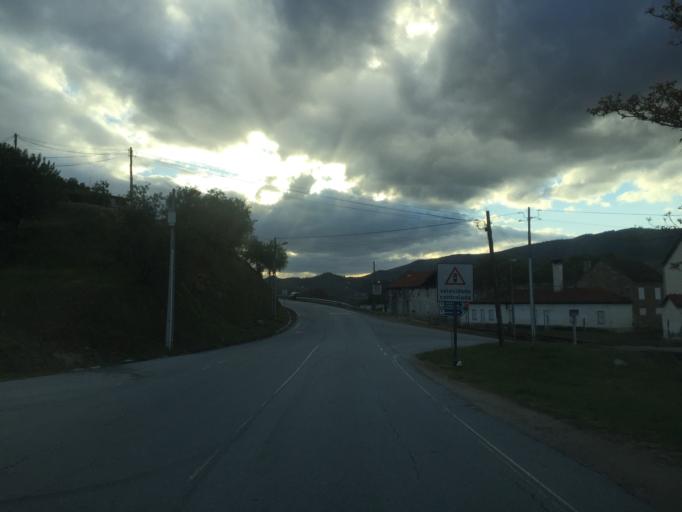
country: PT
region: Braganca
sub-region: Torre de Moncorvo
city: Torre de Moncorvo
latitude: 41.1315
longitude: -7.1187
